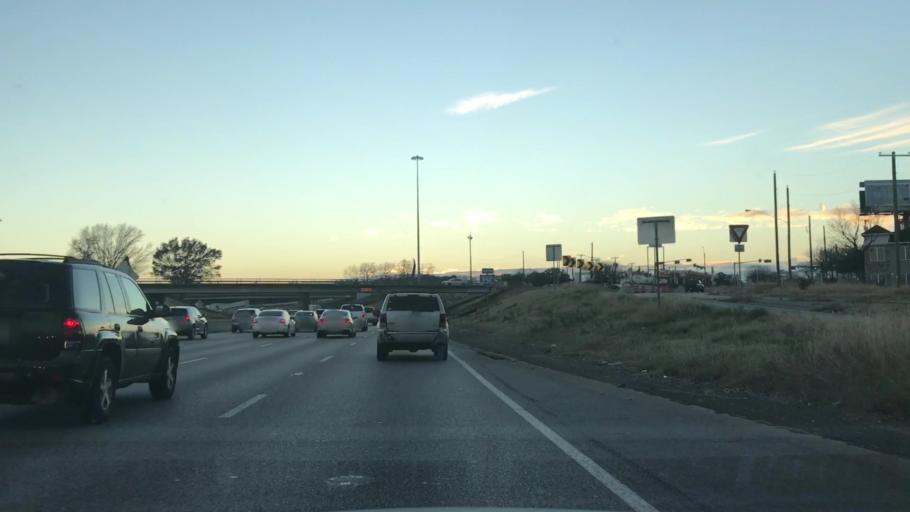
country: US
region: Texas
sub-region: Dallas County
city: Dallas
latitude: 32.7414
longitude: -96.8206
